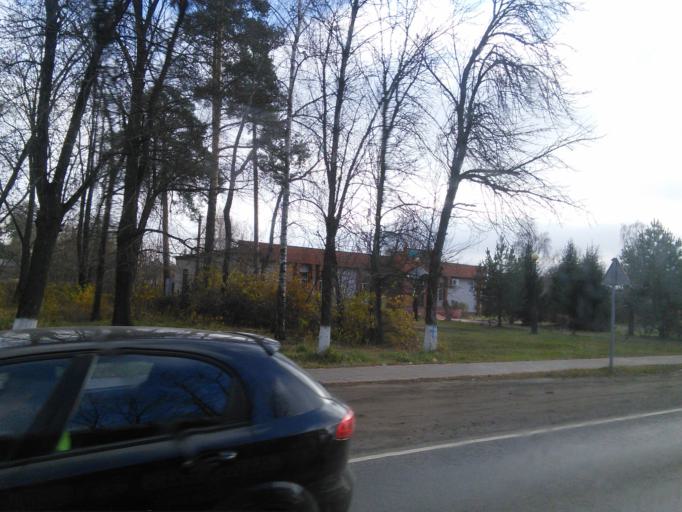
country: RU
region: Moskovskaya
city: Likino-Dulevo
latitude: 55.7106
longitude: 38.9578
